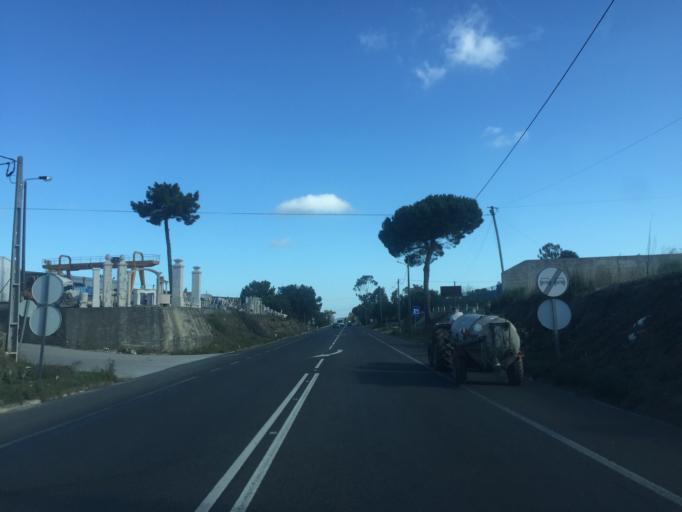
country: PT
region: Leiria
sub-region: Alcobaca
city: Aljubarrota
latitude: 39.5667
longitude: -8.8809
